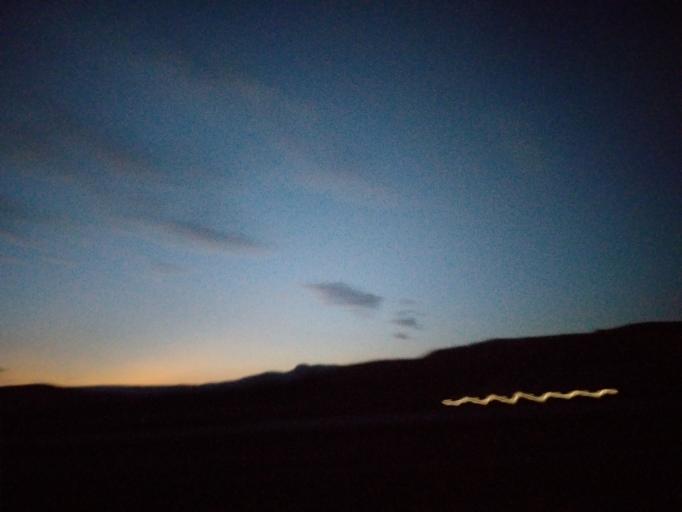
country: TR
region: Ankara
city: Kazan
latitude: 40.1742
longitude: 32.5894
